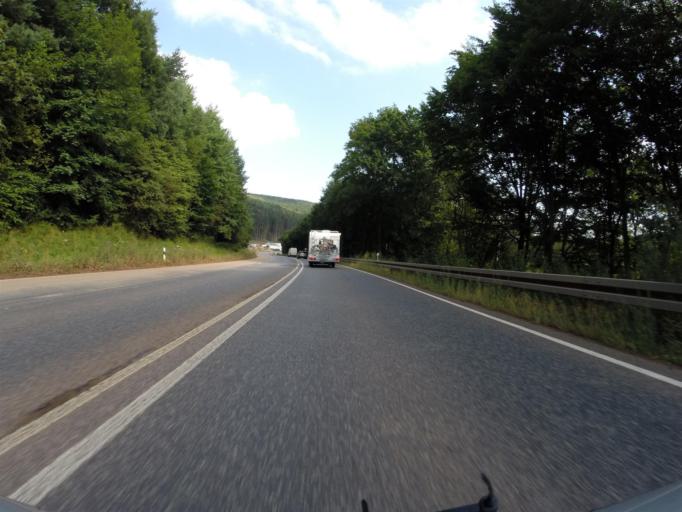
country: DE
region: Hesse
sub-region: Regierungsbezirk Kassel
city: Helsa
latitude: 51.2318
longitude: 9.6733
